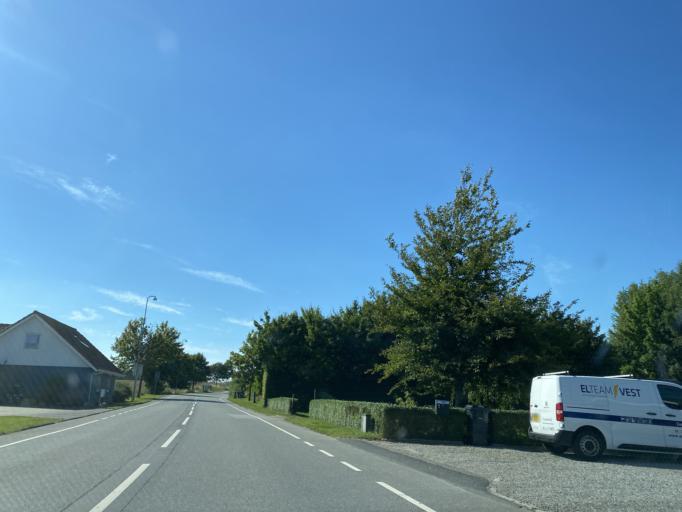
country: DK
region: Central Jutland
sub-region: Hedensted Kommune
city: Torring
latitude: 55.8624
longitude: 9.4124
